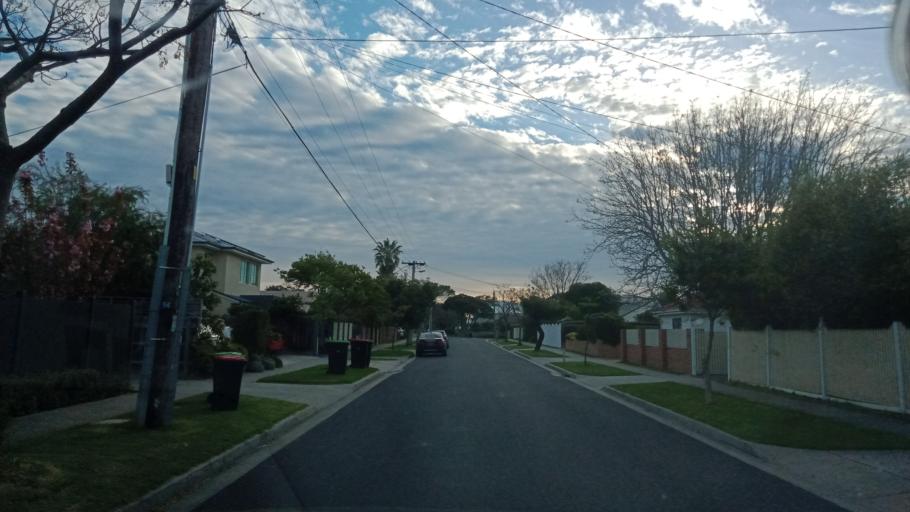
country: AU
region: Victoria
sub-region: Kingston
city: Chelsea
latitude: -38.0425
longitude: 145.1233
